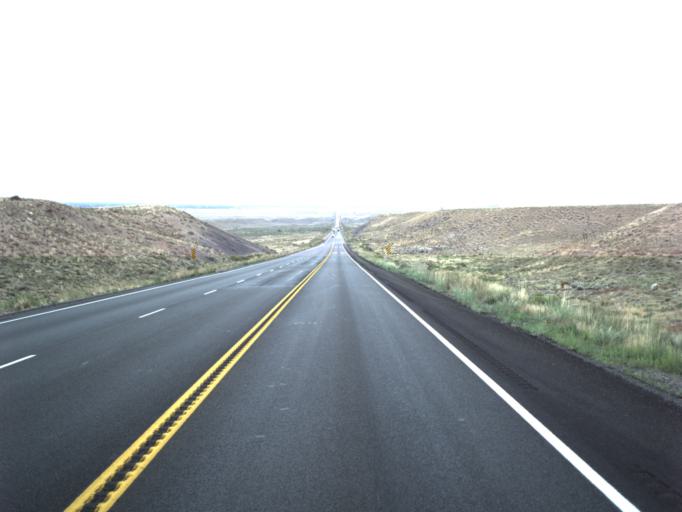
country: US
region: Utah
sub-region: Carbon County
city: East Carbon City
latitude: 39.4770
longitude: -110.5061
